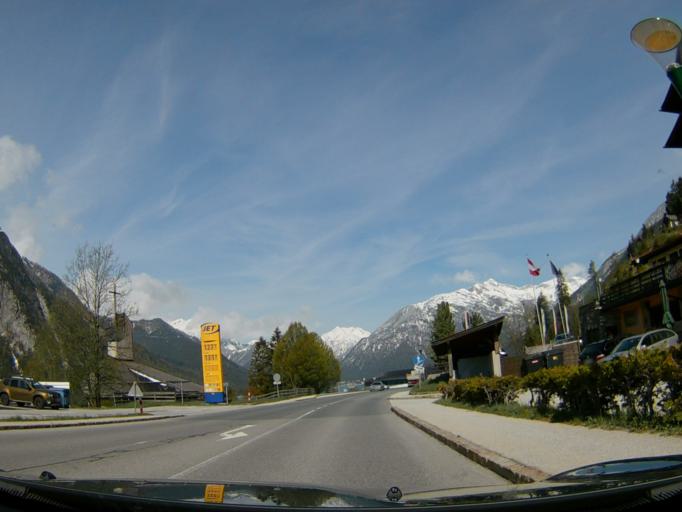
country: AT
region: Tyrol
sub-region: Politischer Bezirk Schwaz
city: Jenbach
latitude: 47.4237
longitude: 11.7518
